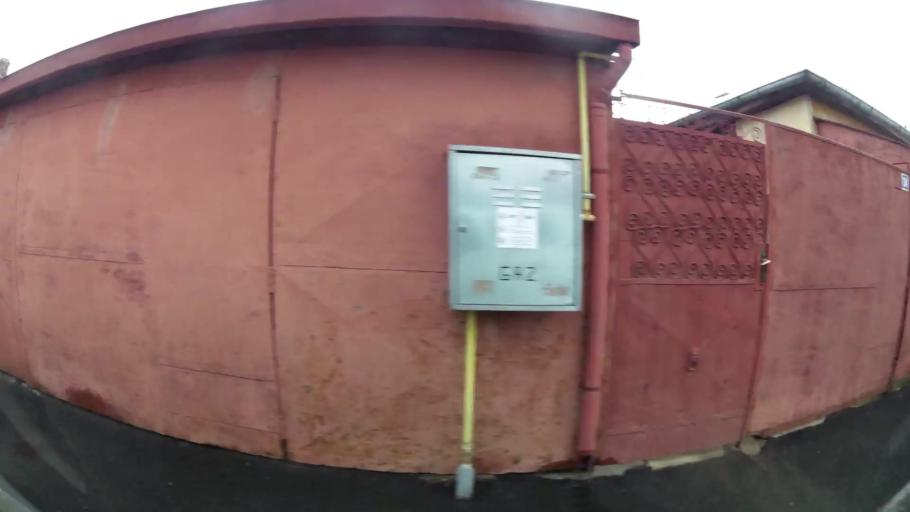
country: RO
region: Ilfov
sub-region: Comuna Pantelimon
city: Pantelimon
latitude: 44.4570
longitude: 26.2027
